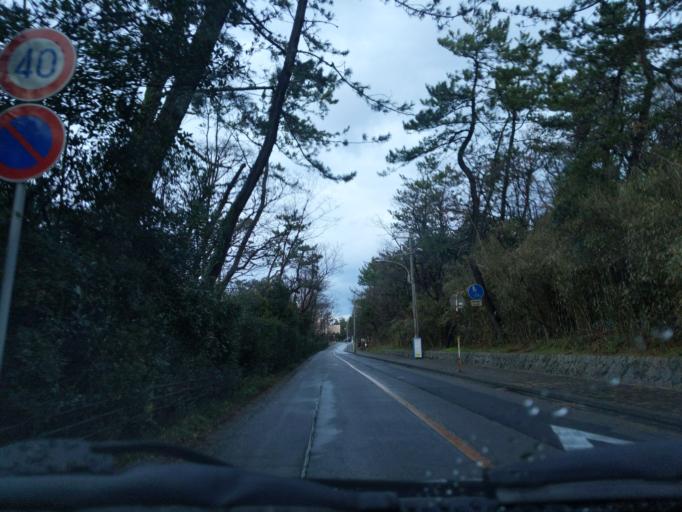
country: JP
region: Niigata
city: Niigata-shi
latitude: 37.9235
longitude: 139.0295
